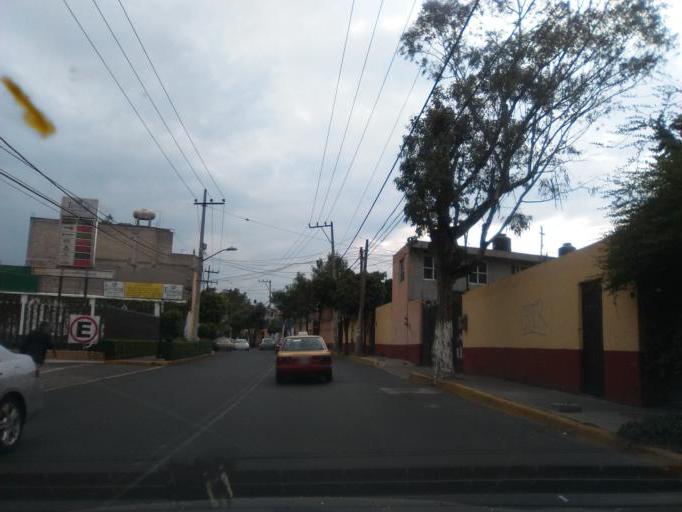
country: MX
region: Mexico City
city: Col. Bosques de las Lomas
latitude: 19.3592
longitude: -99.2554
